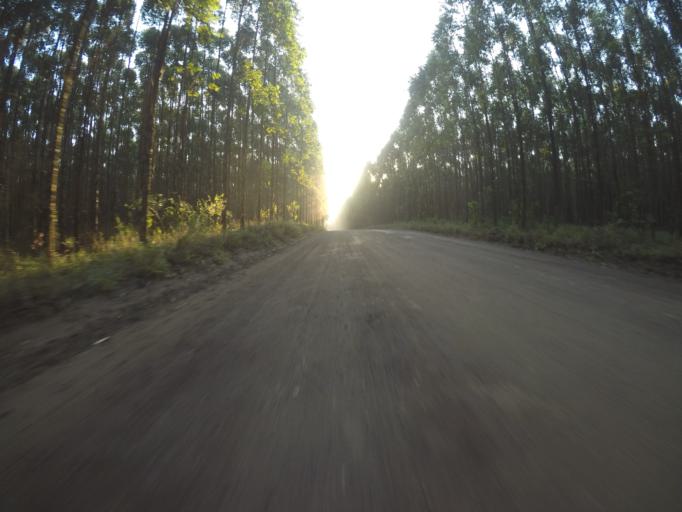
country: ZA
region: KwaZulu-Natal
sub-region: uThungulu District Municipality
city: KwaMbonambi
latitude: -28.6726
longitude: 32.0895
